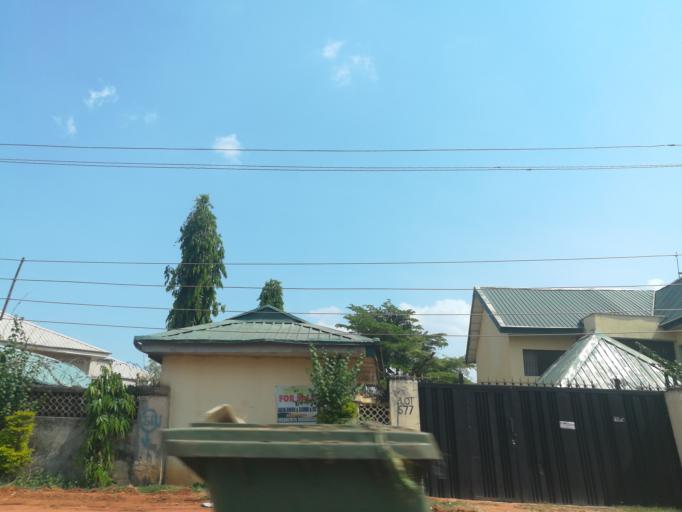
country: NG
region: Abuja Federal Capital Territory
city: Abuja
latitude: 9.0504
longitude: 7.4482
